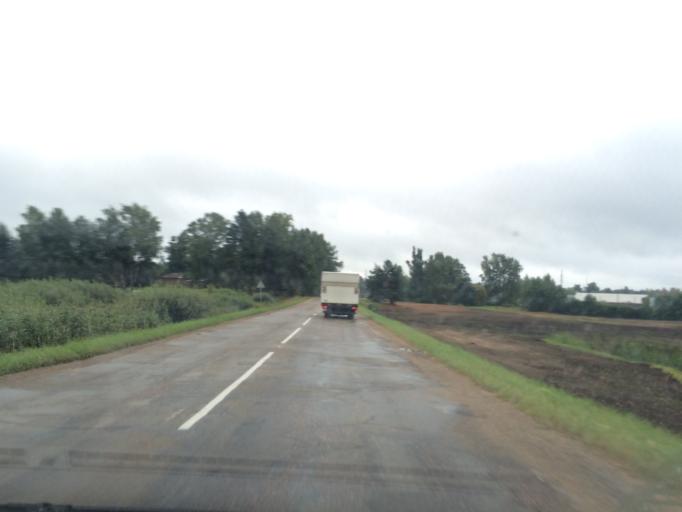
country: LV
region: Ikskile
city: Ikskile
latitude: 56.8495
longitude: 24.5036
